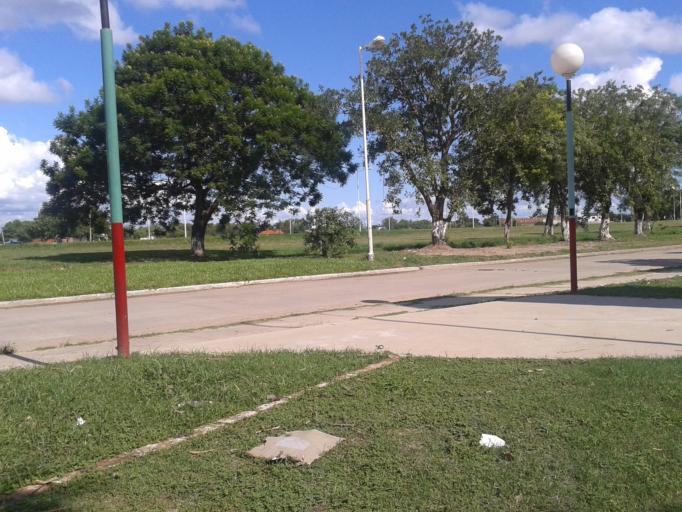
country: AR
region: Formosa
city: Clorinda
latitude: -25.2854
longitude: -57.7346
